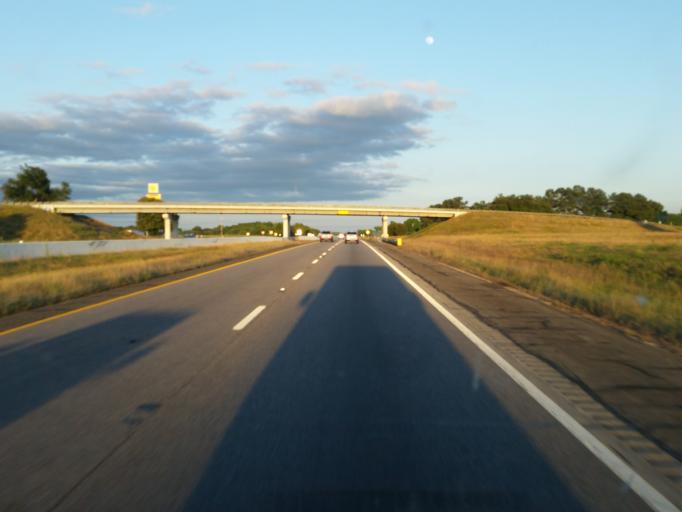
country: US
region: Texas
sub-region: Van Zandt County
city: Canton
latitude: 32.5429
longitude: -95.7588
